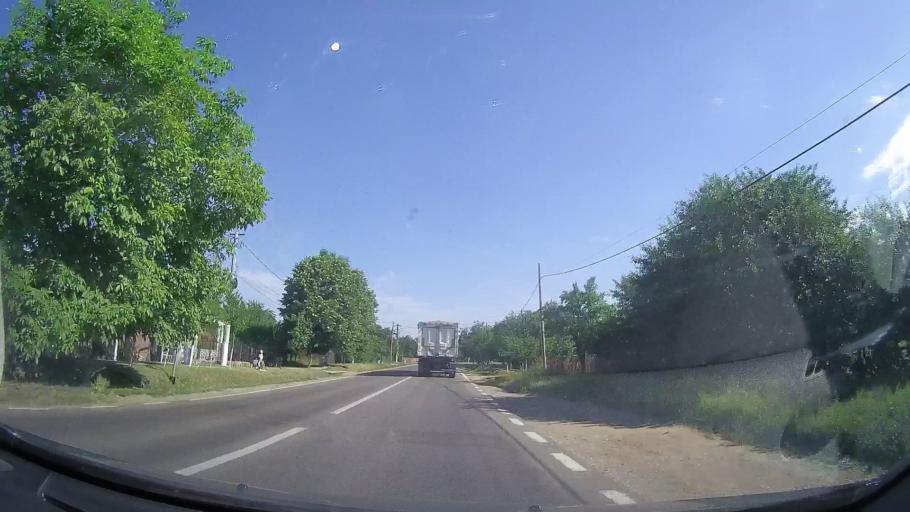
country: RO
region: Prahova
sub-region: Comuna Magurele
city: Magurele
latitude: 45.1130
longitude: 26.0351
